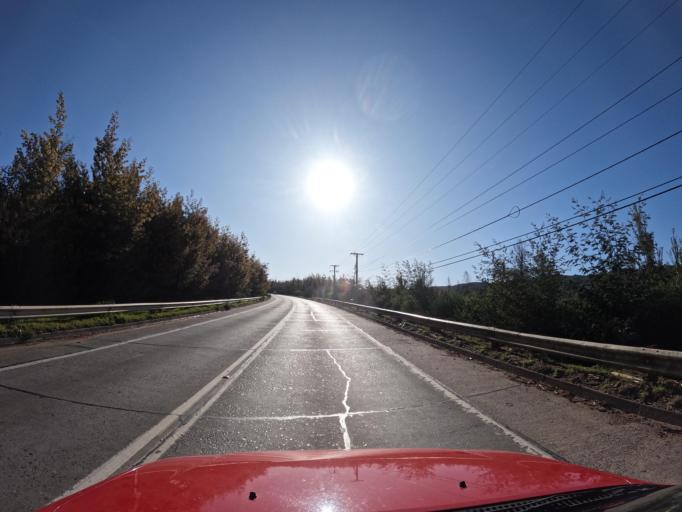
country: CL
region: Maule
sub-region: Provincia de Talca
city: Constitucion
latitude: -35.4448
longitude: -72.2961
